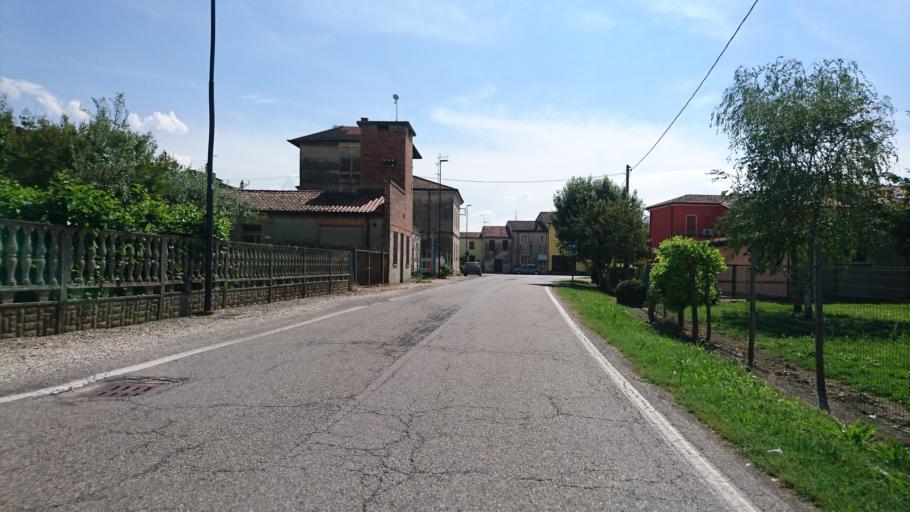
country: IT
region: Veneto
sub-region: Provincia di Rovigo
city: Castelmassa
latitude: 45.0596
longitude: 11.3321
